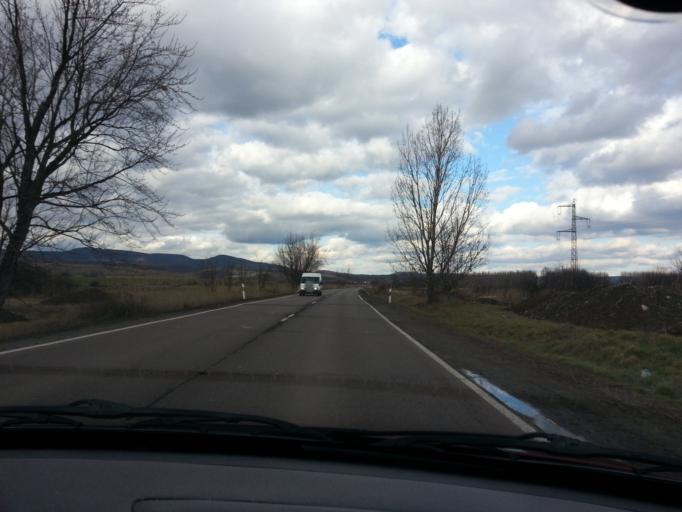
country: HU
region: Nograd
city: Paszto
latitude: 47.9271
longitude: 19.6846
